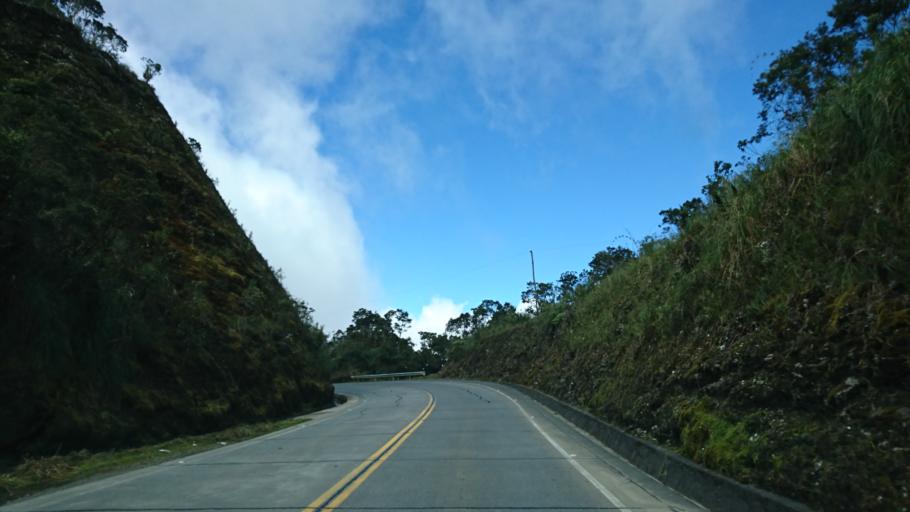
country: BO
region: La Paz
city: Coroico
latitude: -16.2856
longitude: -67.8446
